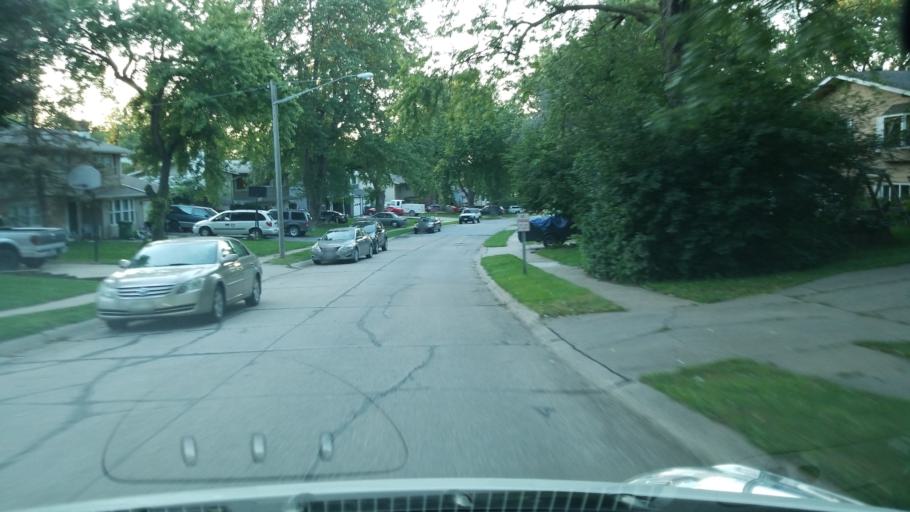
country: US
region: Nebraska
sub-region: Sarpy County
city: Bellevue
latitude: 41.1488
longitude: -95.9107
